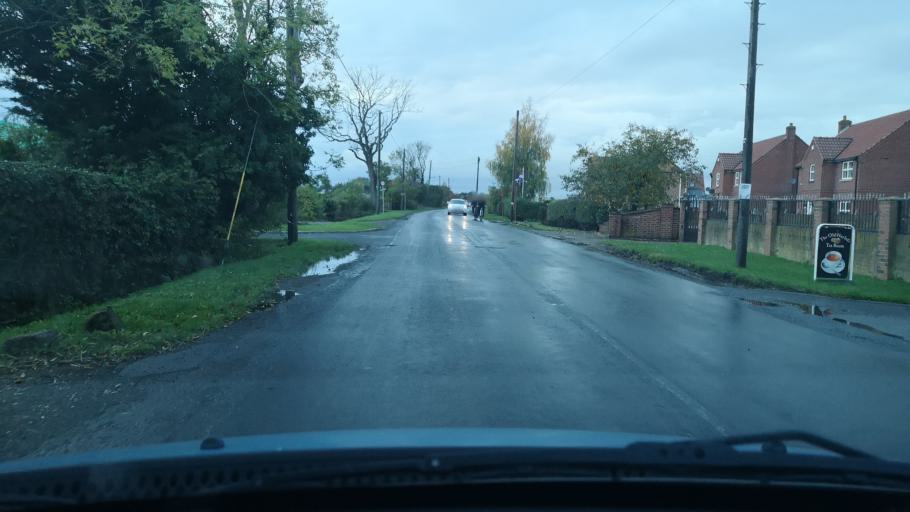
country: GB
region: England
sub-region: Doncaster
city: Moss
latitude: 53.6219
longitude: -1.0996
